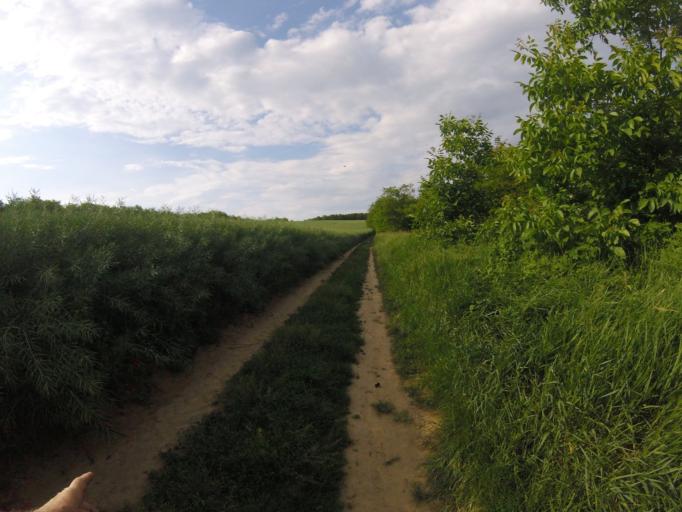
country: HU
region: Zala
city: Zalaszentgrot
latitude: 46.8772
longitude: 17.1231
